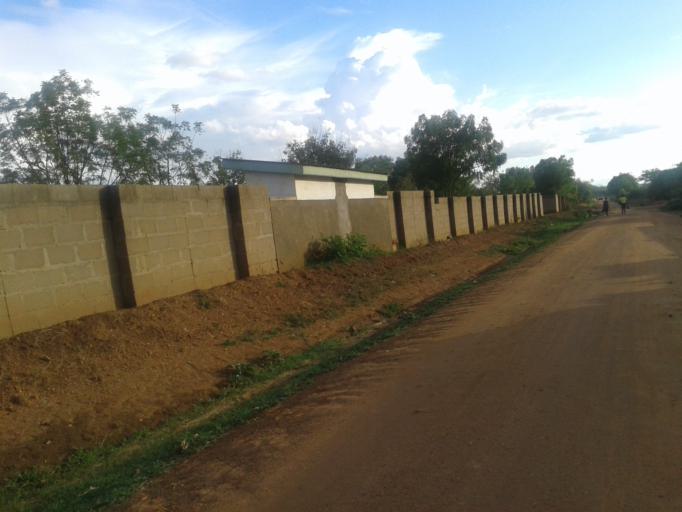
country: UG
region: Northern Region
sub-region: Kotido District
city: Kotido
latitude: 3.0007
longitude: 34.1071
